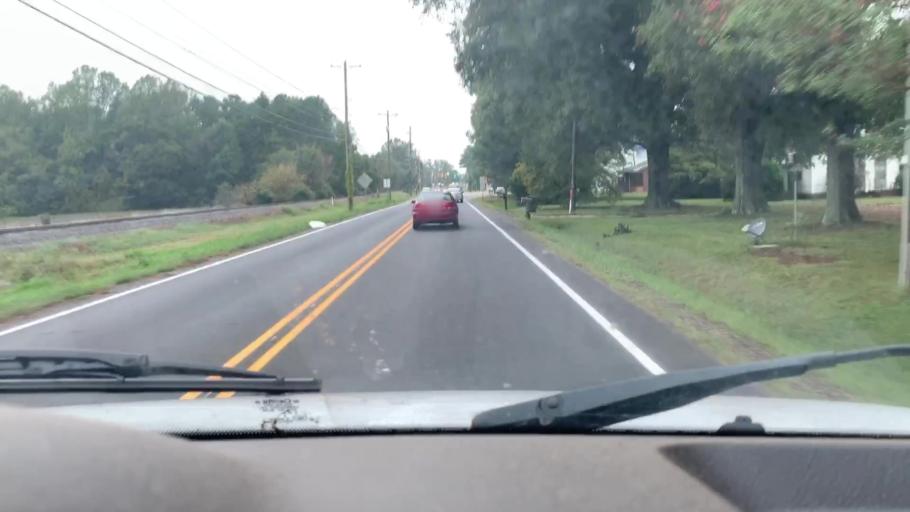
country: US
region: North Carolina
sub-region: Gaston County
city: Davidson
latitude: 35.5332
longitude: -80.8461
